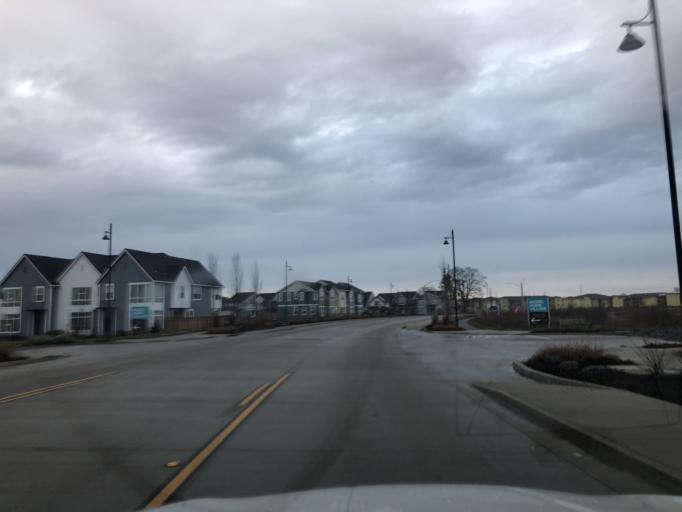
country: US
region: Oregon
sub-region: Washington County
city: Aloha
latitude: 45.4933
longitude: -122.9039
